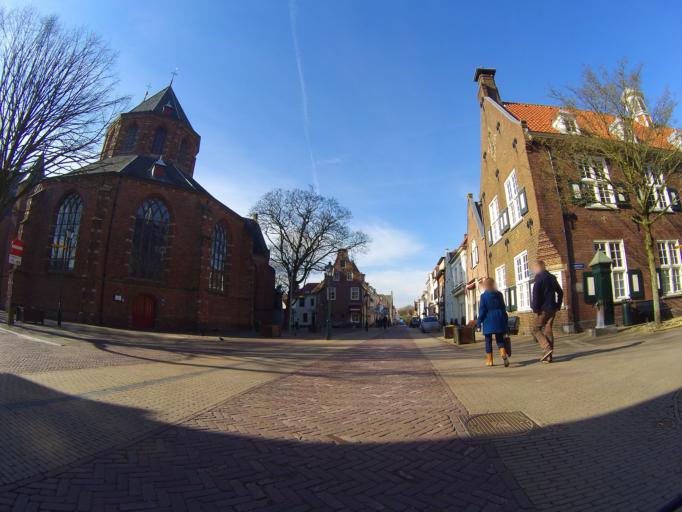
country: NL
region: North Holland
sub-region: Gemeente Naarden
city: Naarden
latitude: 52.2957
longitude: 5.1636
